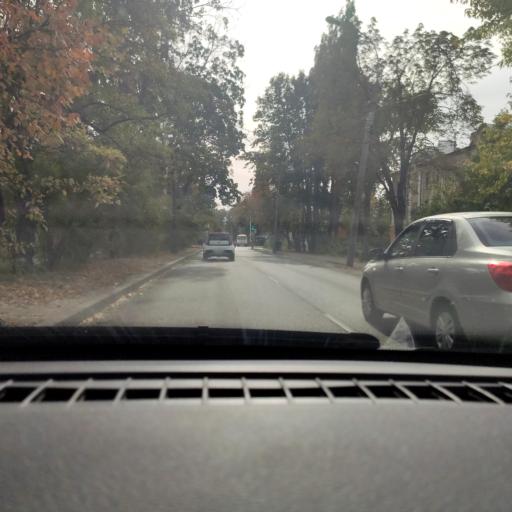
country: RU
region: Voronezj
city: Voronezh
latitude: 51.7151
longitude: 39.2230
